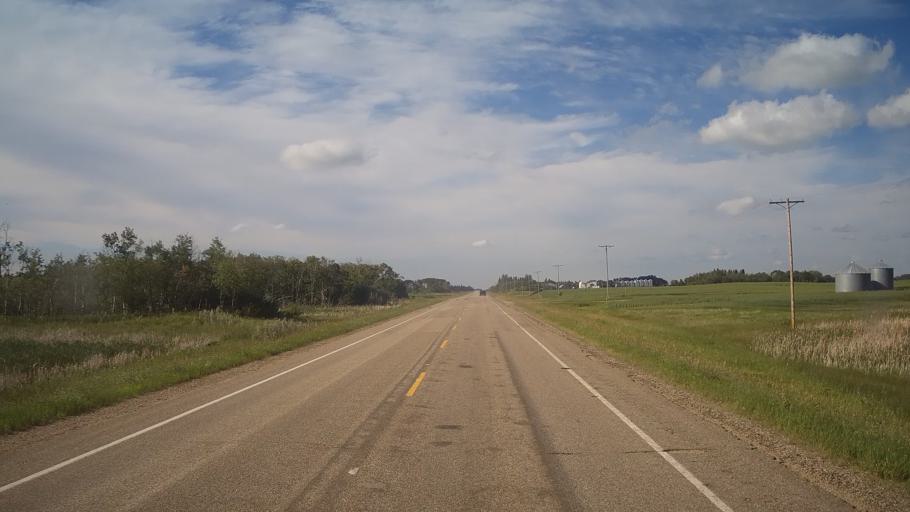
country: CA
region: Saskatchewan
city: Foam Lake
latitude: 51.5819
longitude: -103.8458
